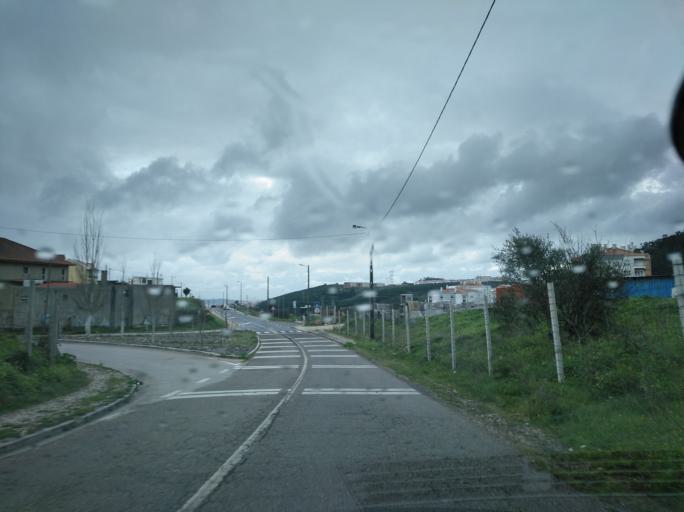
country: PT
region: Lisbon
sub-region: Odivelas
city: Canecas
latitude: 38.7958
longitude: -9.2299
